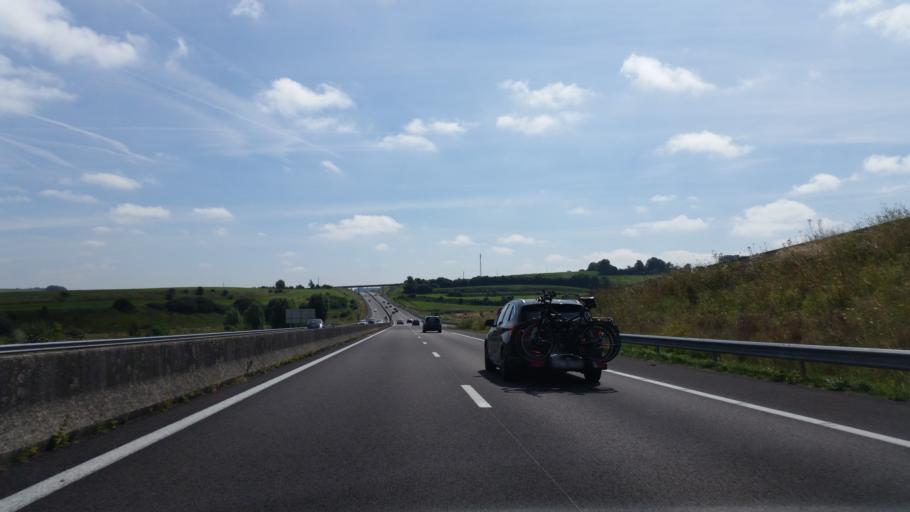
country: FR
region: Haute-Normandie
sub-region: Departement de la Seine-Maritime
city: Neufchatel-en-Bray
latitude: 49.7427
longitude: 1.5331
